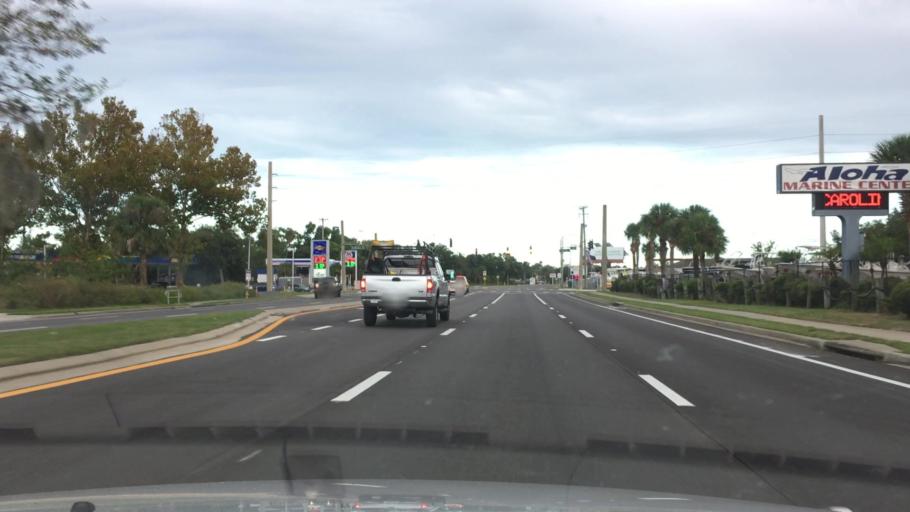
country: US
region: Florida
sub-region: Volusia County
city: Holly Hill
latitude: 29.2426
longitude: -81.0616
